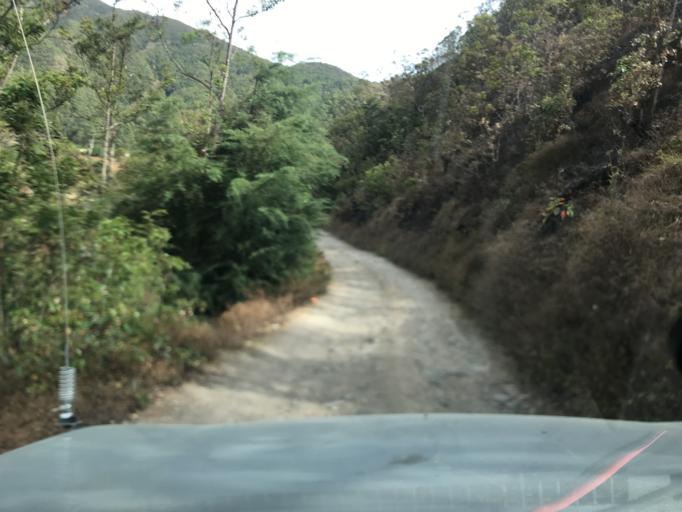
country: TL
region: Ainaro
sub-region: Ainaro
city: Ainaro
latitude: -8.8857
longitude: 125.5446
